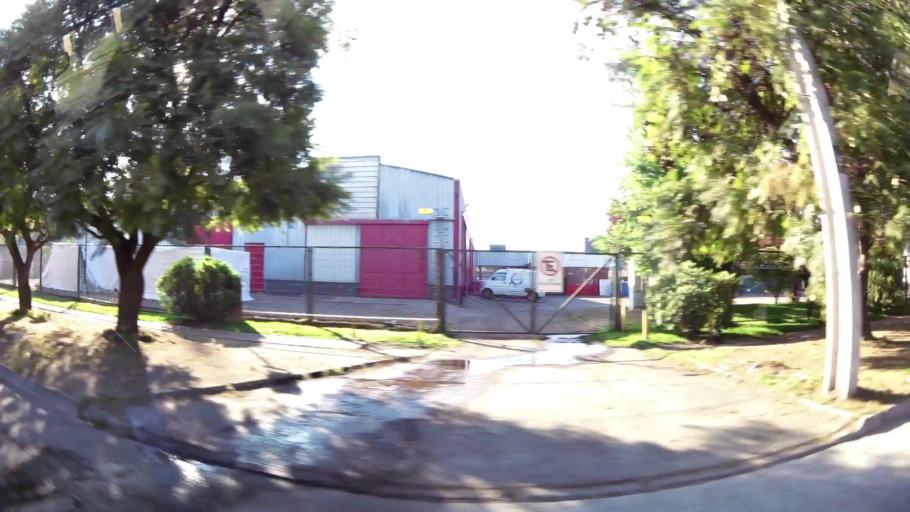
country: CL
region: Santiago Metropolitan
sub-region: Provincia de Santiago
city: Santiago
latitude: -33.3772
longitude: -70.6522
